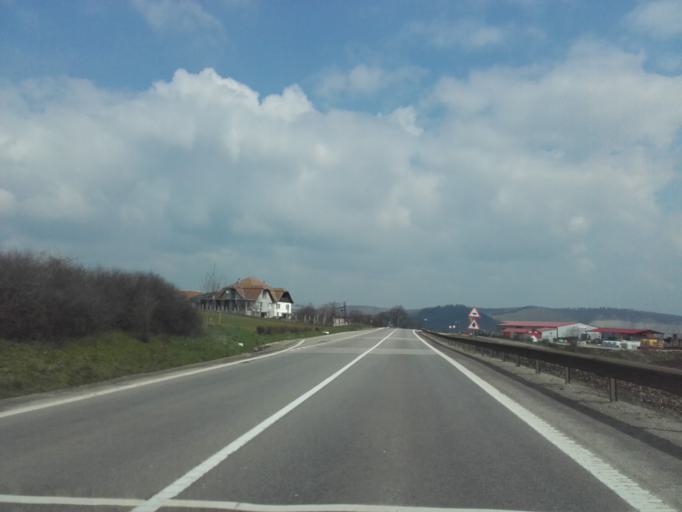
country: RO
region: Mures
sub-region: Comuna Ludus
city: Ludus
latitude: 46.4791
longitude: 24.1240
